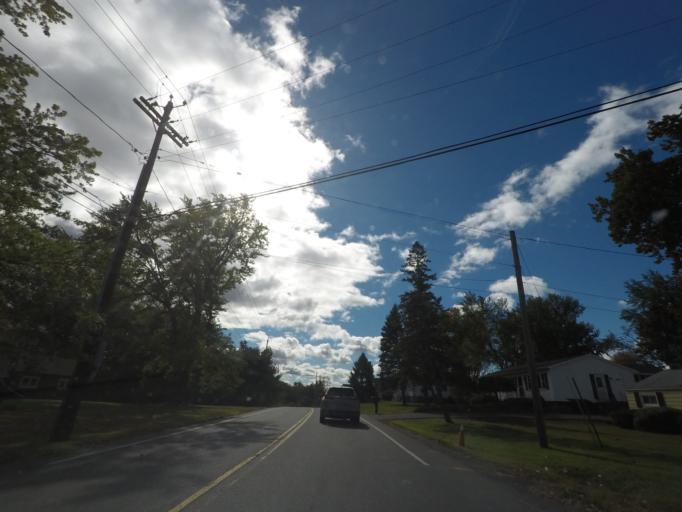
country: US
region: New York
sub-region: Albany County
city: Cohoes
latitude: 42.7793
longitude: -73.7311
